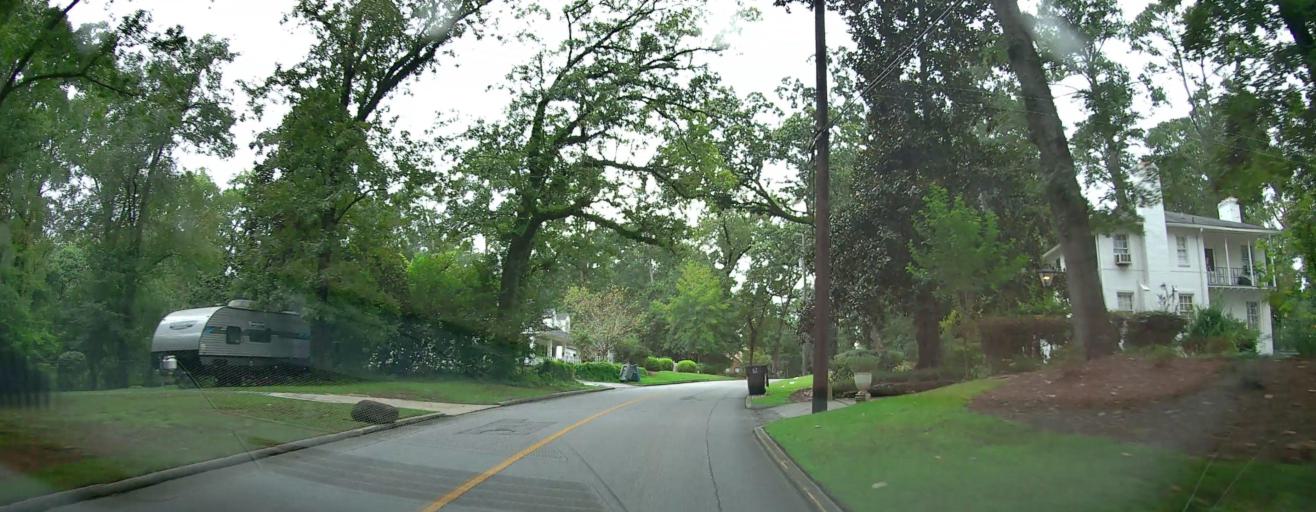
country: US
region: Georgia
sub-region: Bibb County
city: Macon
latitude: 32.8555
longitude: -83.6728
